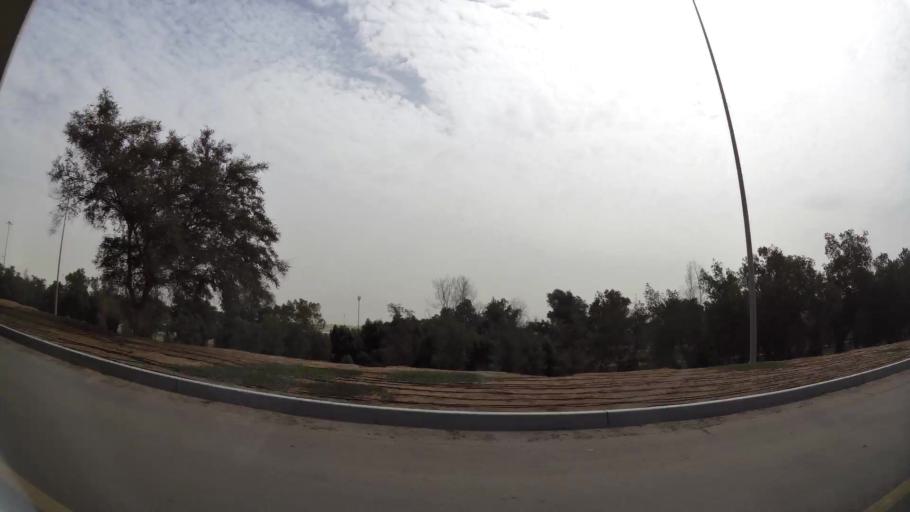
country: AE
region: Abu Dhabi
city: Abu Dhabi
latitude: 24.3900
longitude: 54.5365
